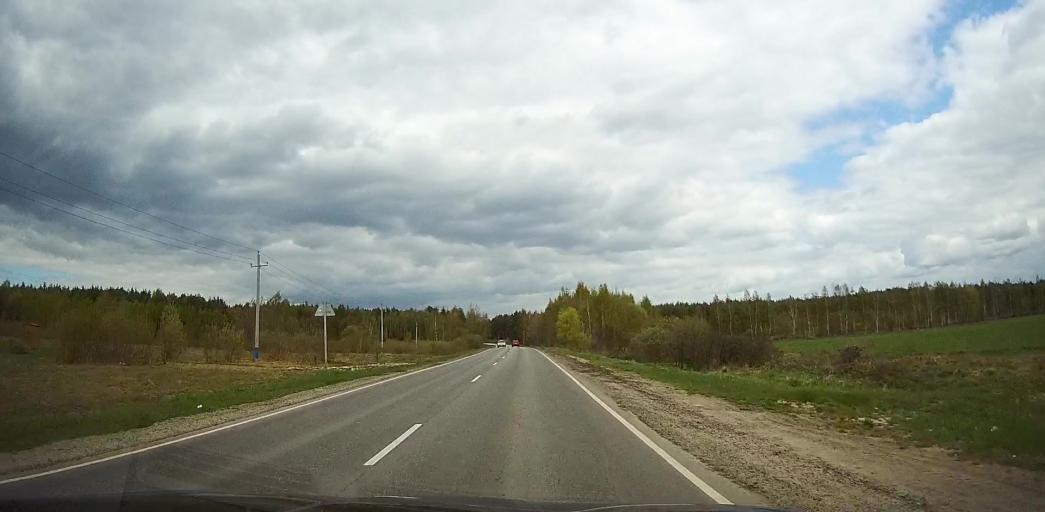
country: RU
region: Moskovskaya
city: Ashitkovo
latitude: 55.4666
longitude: 38.6078
